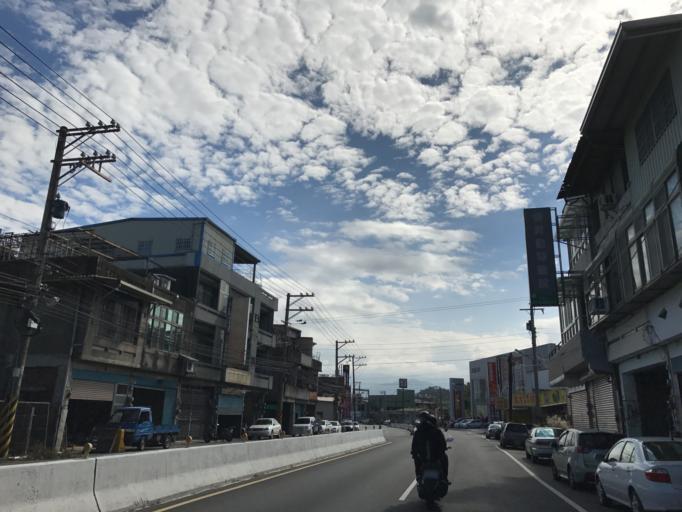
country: TW
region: Taiwan
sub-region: Hsinchu
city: Zhubei
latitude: 24.7556
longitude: 121.0707
